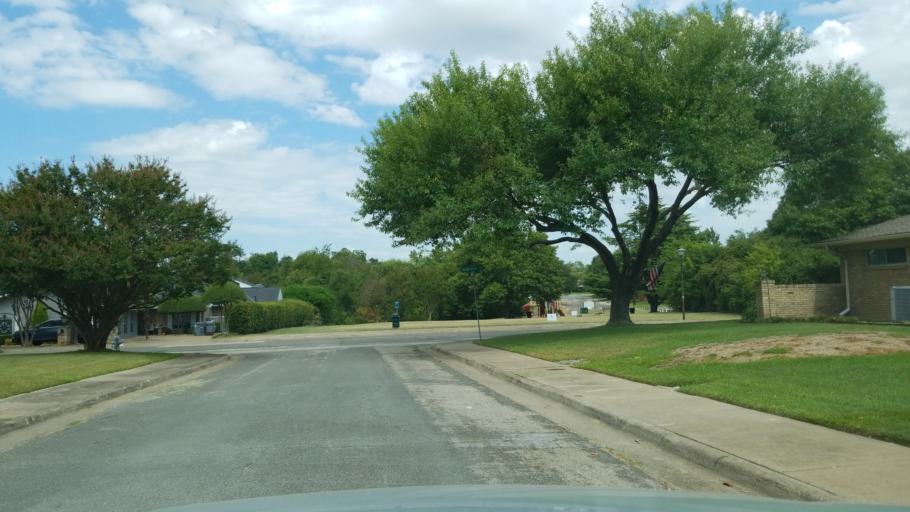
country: US
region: Texas
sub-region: Dallas County
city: Addison
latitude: 32.9516
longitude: -96.7814
